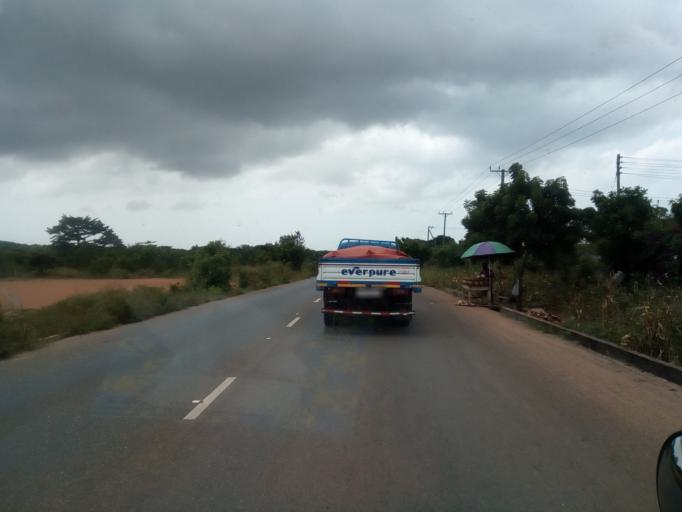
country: GH
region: Greater Accra
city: Dome
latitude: 5.6554
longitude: -0.2053
